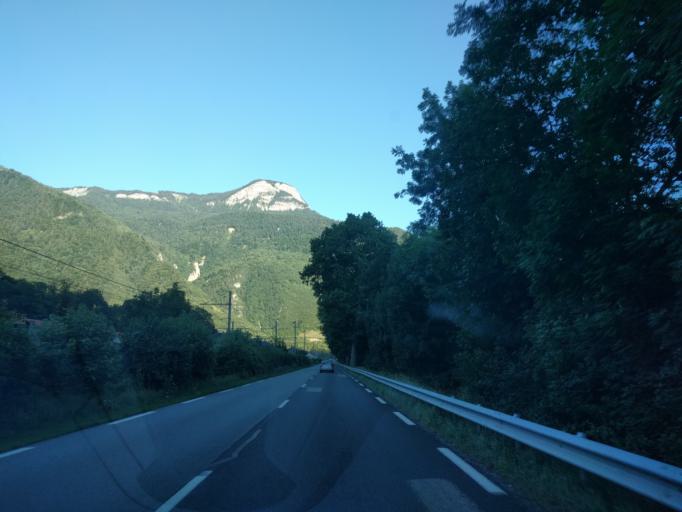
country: FR
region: Rhone-Alpes
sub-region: Departement de la Savoie
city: La Chambre
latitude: 45.3557
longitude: 6.2968
